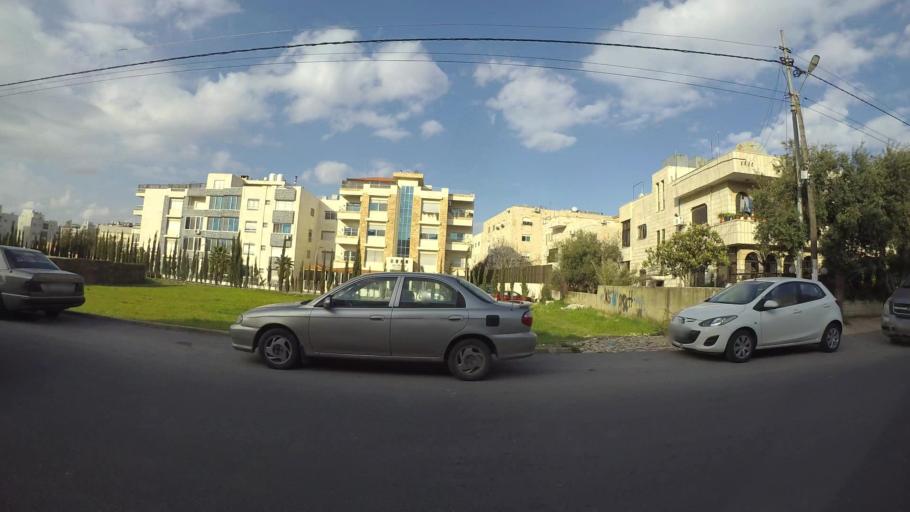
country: JO
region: Amman
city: Umm as Summaq
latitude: 31.8994
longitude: 35.8575
